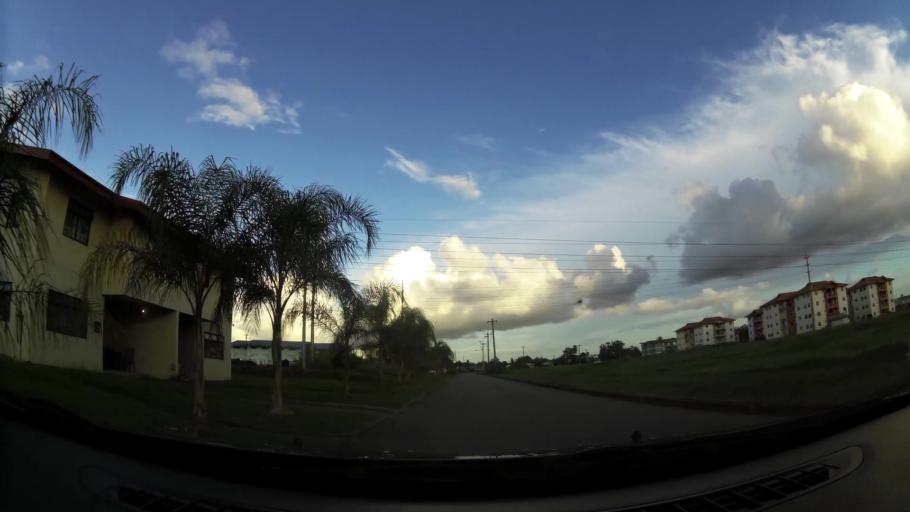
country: TT
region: Tunapuna/Piarco
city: Arouca
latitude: 10.6154
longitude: -61.3544
